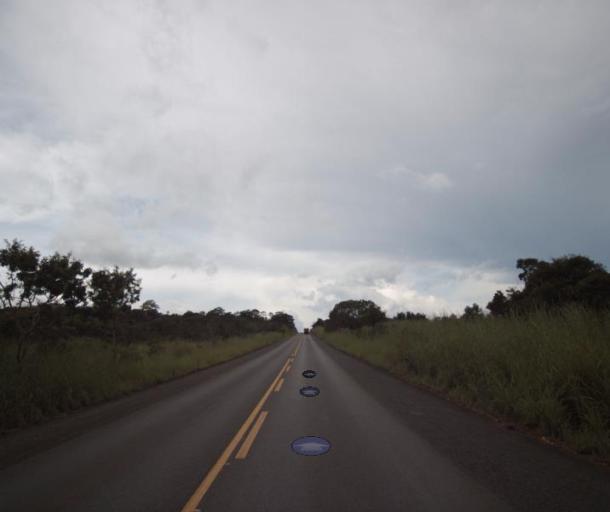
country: BR
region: Goias
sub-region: Niquelandia
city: Niquelandia
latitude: -14.4994
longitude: -48.5019
